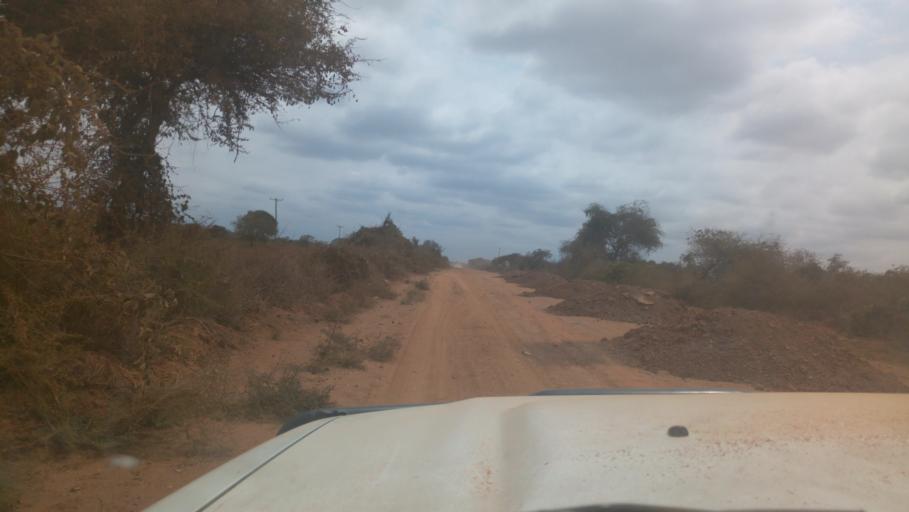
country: KE
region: Makueni
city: Wote
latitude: -1.8651
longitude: 37.9545
